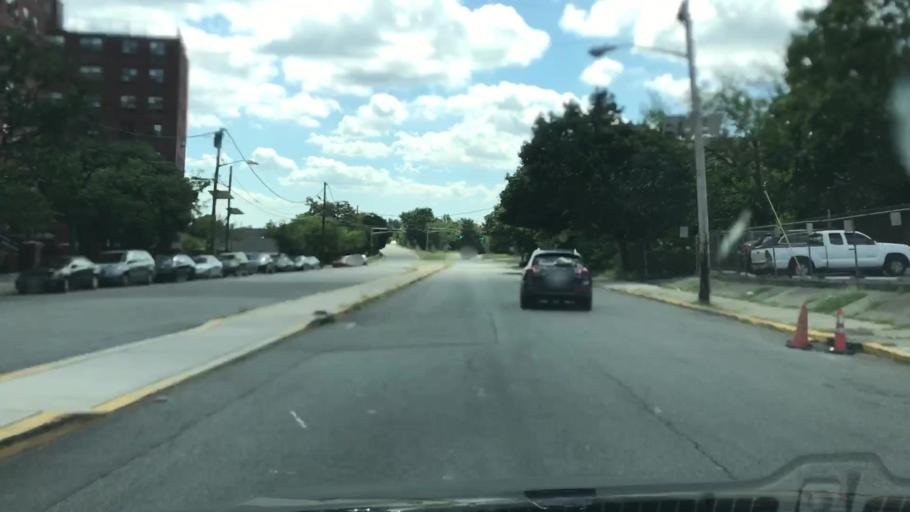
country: US
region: New Jersey
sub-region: Passaic County
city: Passaic
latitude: 40.8603
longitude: -74.1226
